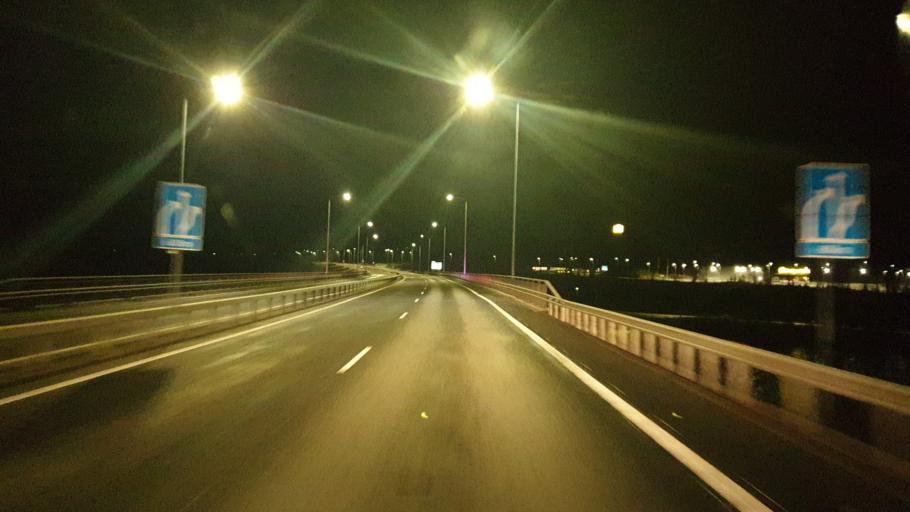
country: FI
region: Central Finland
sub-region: AEaenekoski
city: AEaenekoski
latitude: 62.6035
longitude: 25.6902
